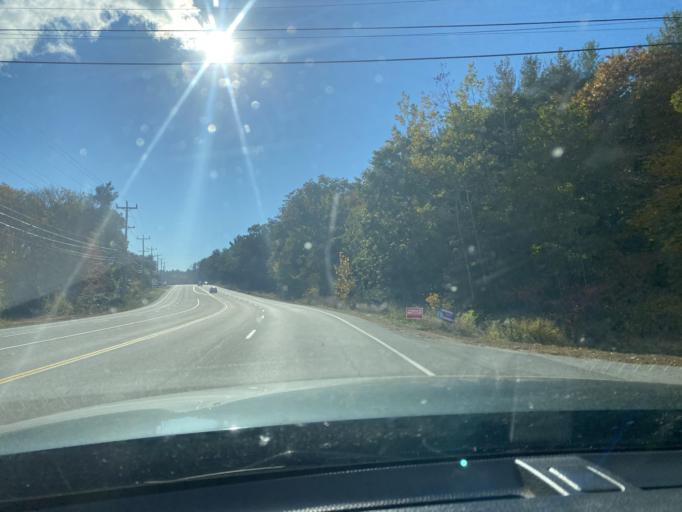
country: US
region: Maine
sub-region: York County
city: Cape Neddick
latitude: 43.1762
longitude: -70.6342
